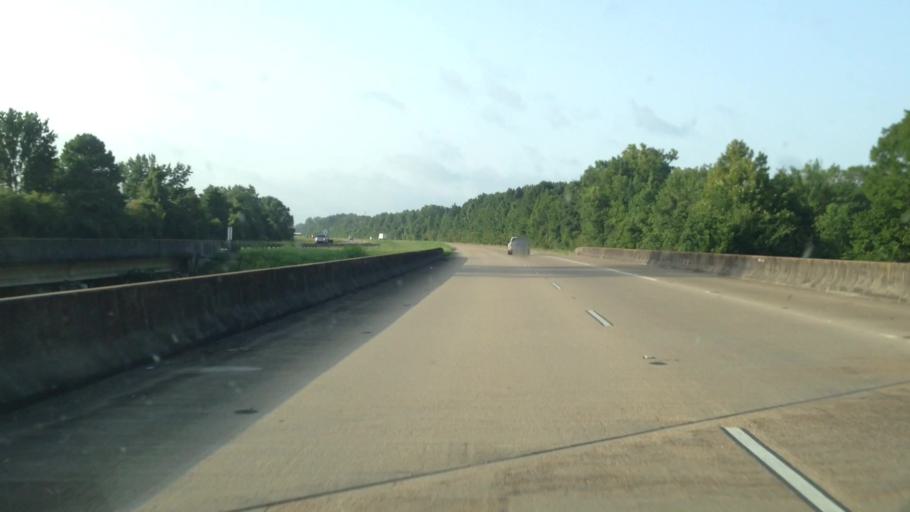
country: US
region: Louisiana
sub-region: Rapides Parish
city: Woodworth
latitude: 31.1433
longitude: -92.4522
